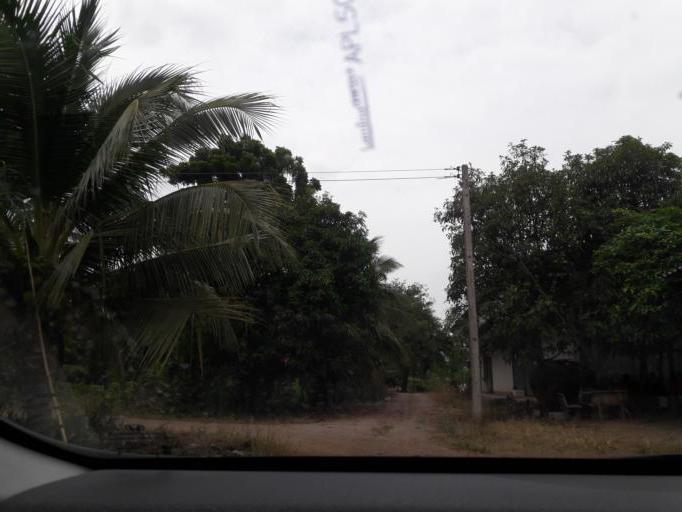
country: TH
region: Ratchaburi
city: Damnoen Saduak
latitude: 13.5664
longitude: 99.9818
